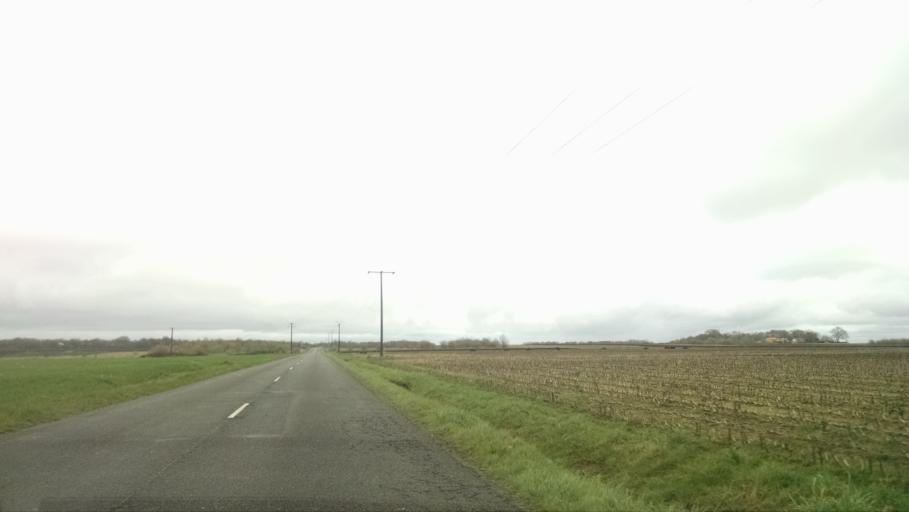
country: FR
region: Pays de la Loire
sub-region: Departement de la Loire-Atlantique
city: Maisdon-sur-Sevre
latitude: 47.1071
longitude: -1.3762
